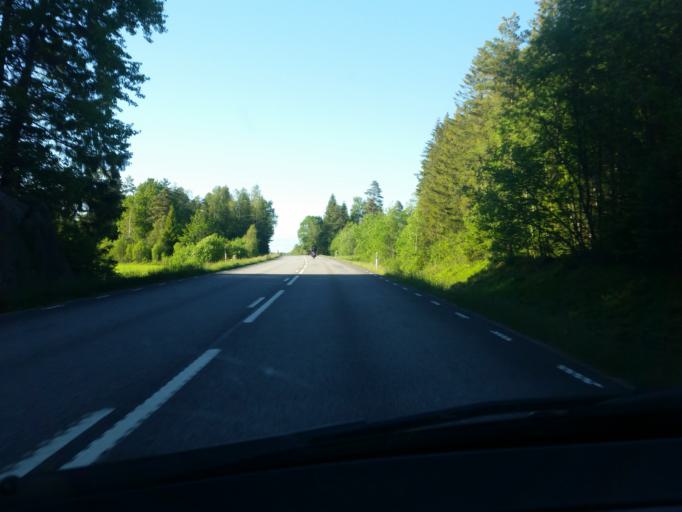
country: SE
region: Vaestra Goetaland
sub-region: Fargelanda Kommun
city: Faergelanda
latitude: 58.5330
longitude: 11.9829
